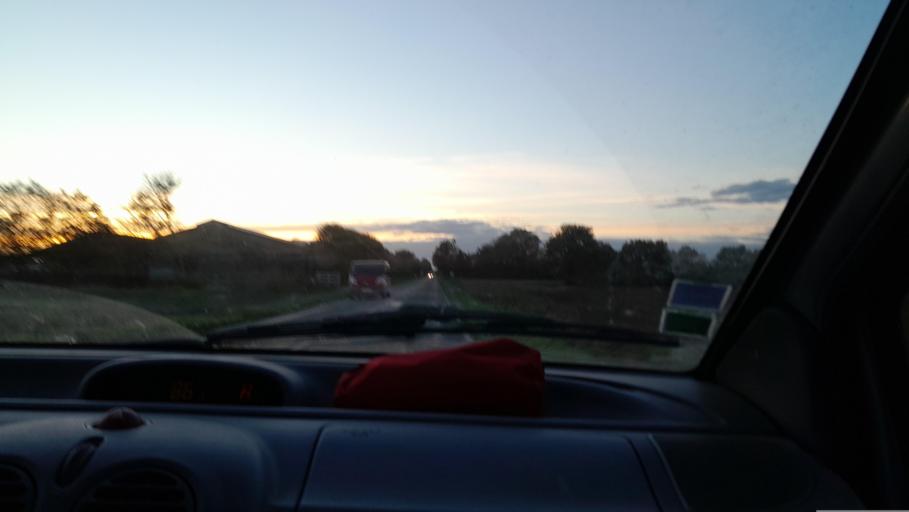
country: FR
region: Pays de la Loire
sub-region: Departement de la Mayenne
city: Ballots
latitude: 47.9016
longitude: -1.1330
